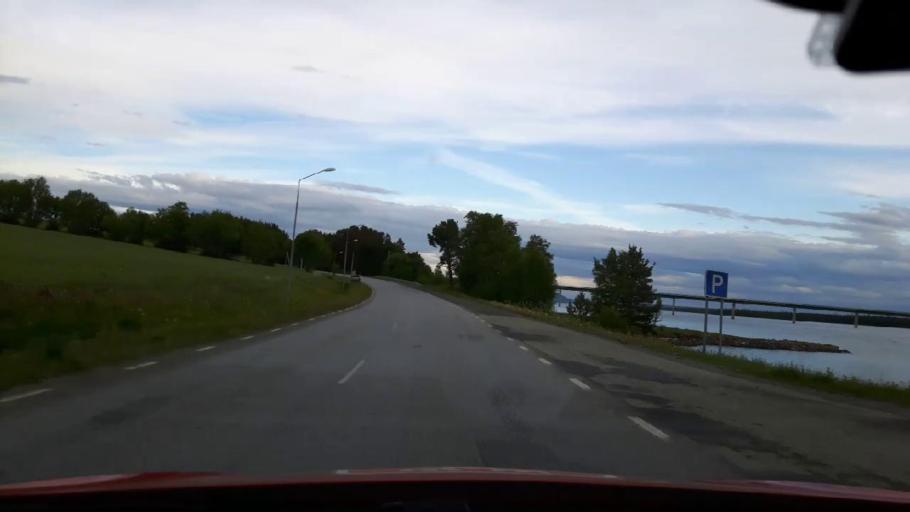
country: SE
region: Jaemtland
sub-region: Bergs Kommun
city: Hoverberg
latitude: 62.9820
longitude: 14.4807
